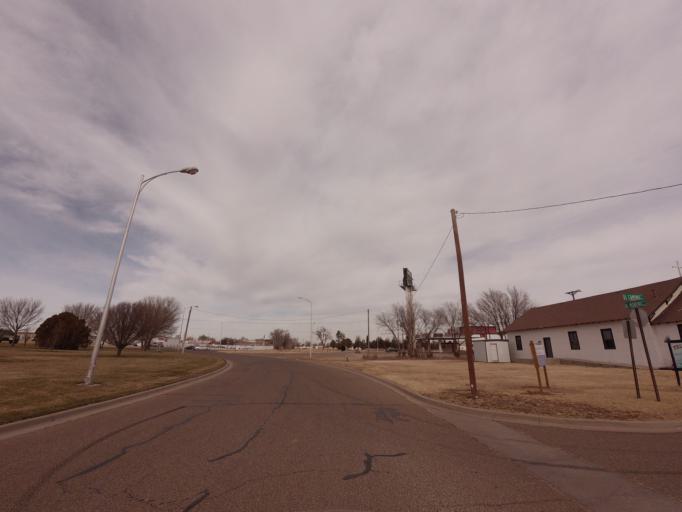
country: US
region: New Mexico
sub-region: Curry County
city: Clovis
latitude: 34.4036
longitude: -103.2450
